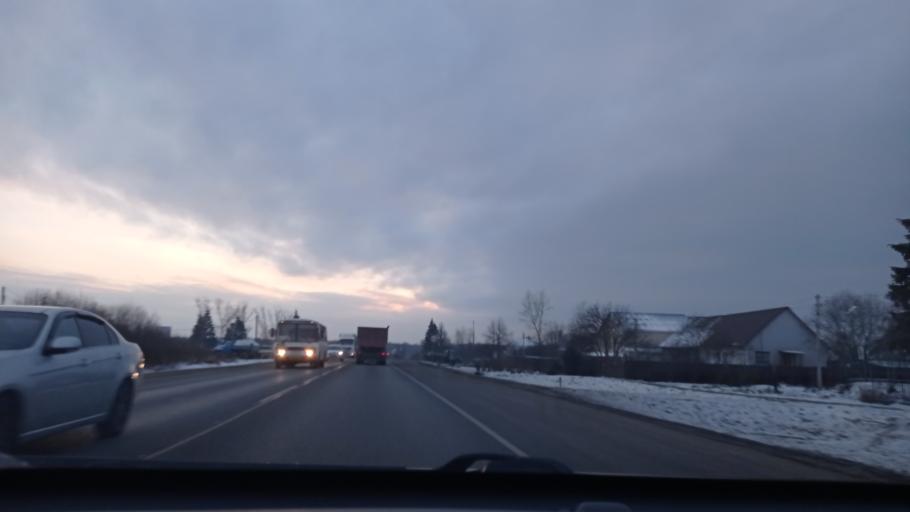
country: RU
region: Moskovskaya
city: Ateptsevo
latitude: 55.1902
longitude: 36.9093
